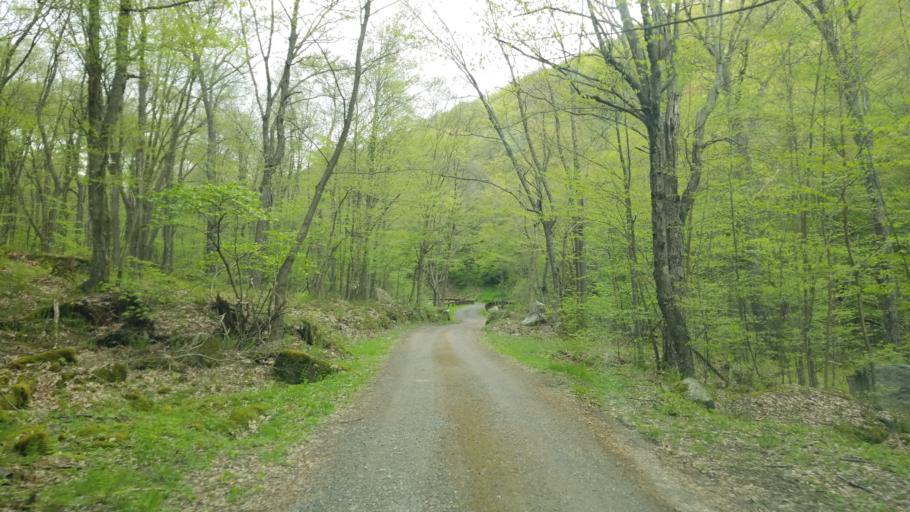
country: US
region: Pennsylvania
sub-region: Clearfield County
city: Shiloh
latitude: 41.2082
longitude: -78.1391
